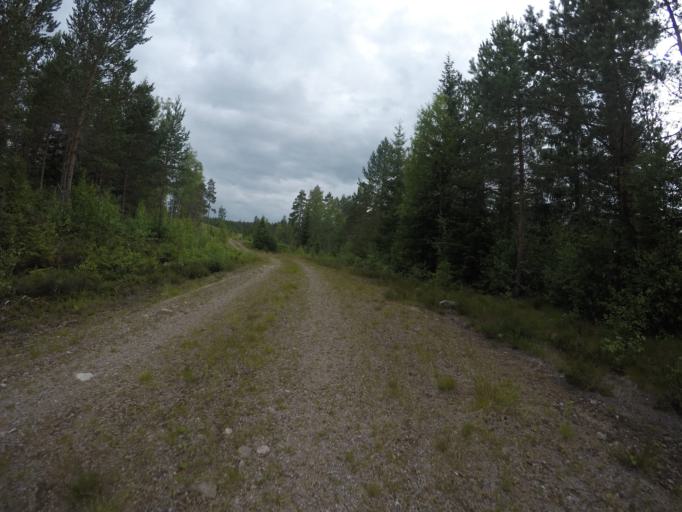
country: SE
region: Vaermland
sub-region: Filipstads Kommun
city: Lesjofors
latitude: 60.2110
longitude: 14.2612
